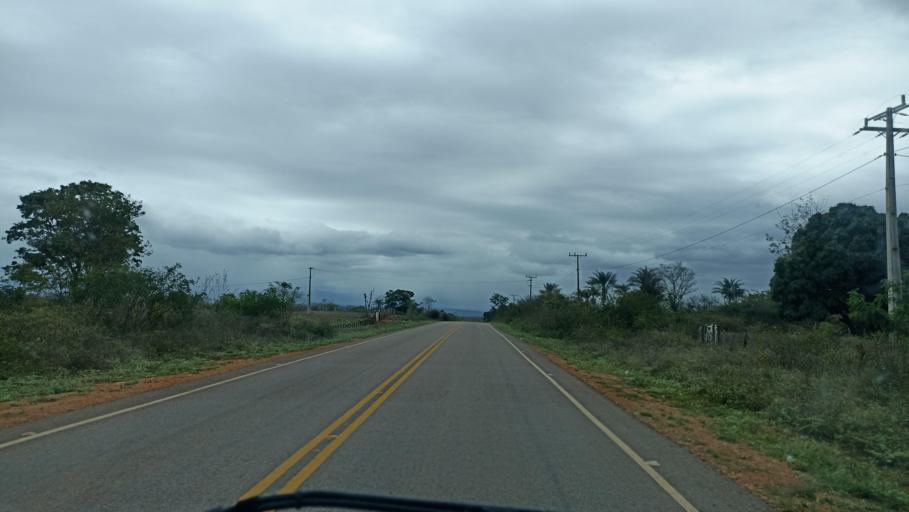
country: BR
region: Bahia
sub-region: Andarai
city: Vera Cruz
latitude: -12.9900
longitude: -41.0031
